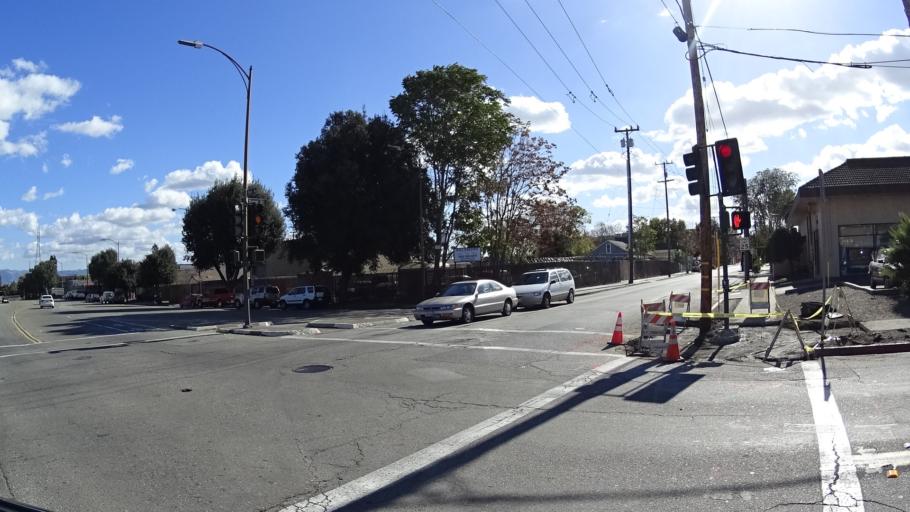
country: US
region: California
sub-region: Santa Clara County
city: Buena Vista
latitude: 37.3263
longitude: -121.9063
